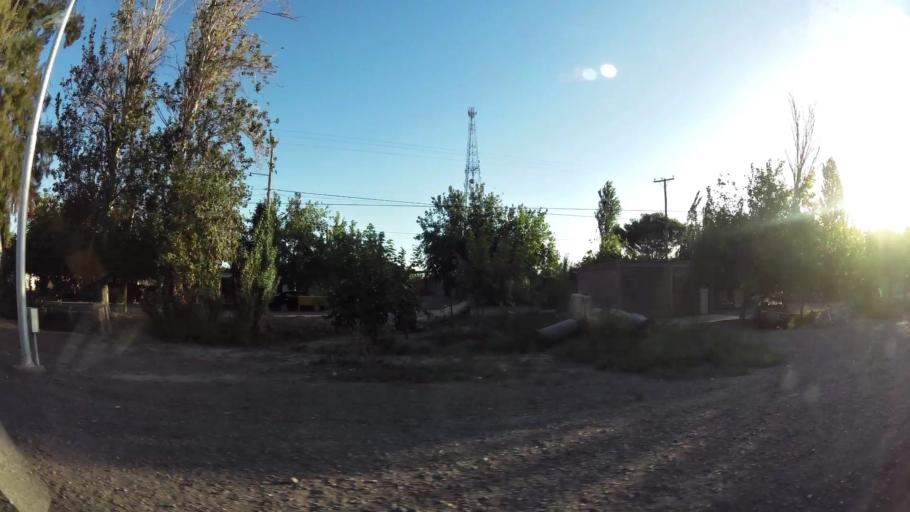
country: AR
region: San Juan
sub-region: Departamento de Santa Lucia
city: Santa Lucia
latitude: -31.5512
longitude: -68.4800
